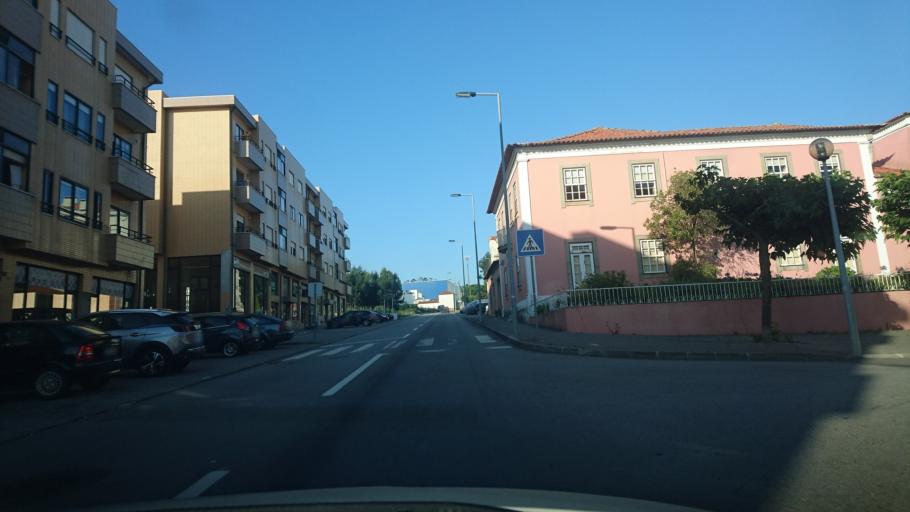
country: PT
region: Aveiro
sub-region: Ovar
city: Esmoriz
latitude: 40.9650
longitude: -8.6205
